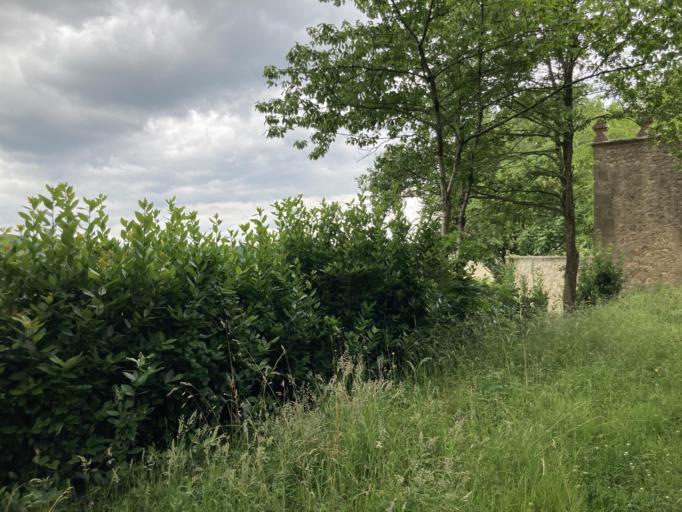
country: FR
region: Aquitaine
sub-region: Departement des Landes
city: Mugron
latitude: 43.7559
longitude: -0.7576
